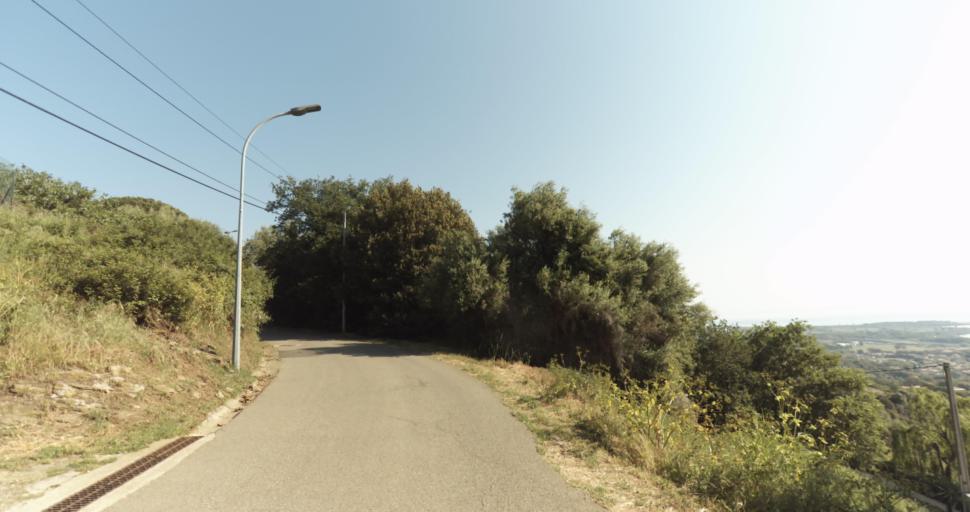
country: FR
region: Corsica
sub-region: Departement de la Haute-Corse
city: Biguglia
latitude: 42.6288
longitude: 9.4188
